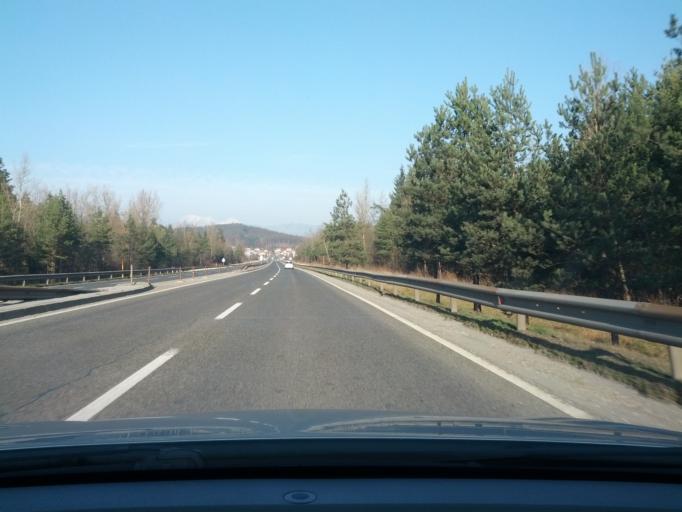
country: SI
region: Ljubljana
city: Ljubljana
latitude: 46.0895
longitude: 14.5336
